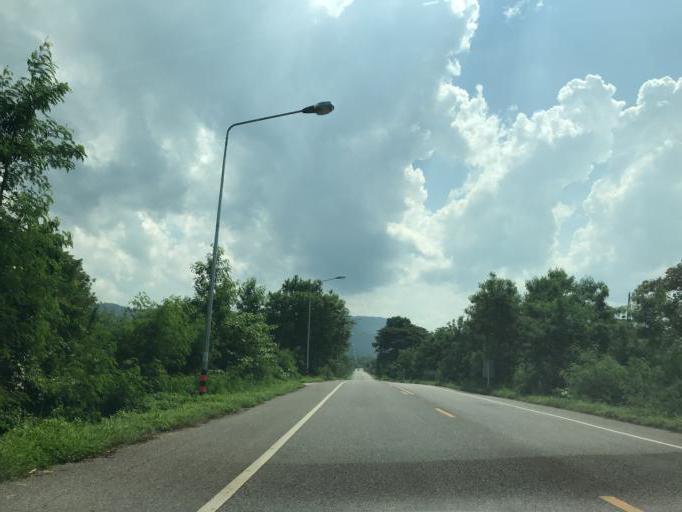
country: TH
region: Phayao
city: Phayao
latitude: 19.0824
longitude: 99.8768
